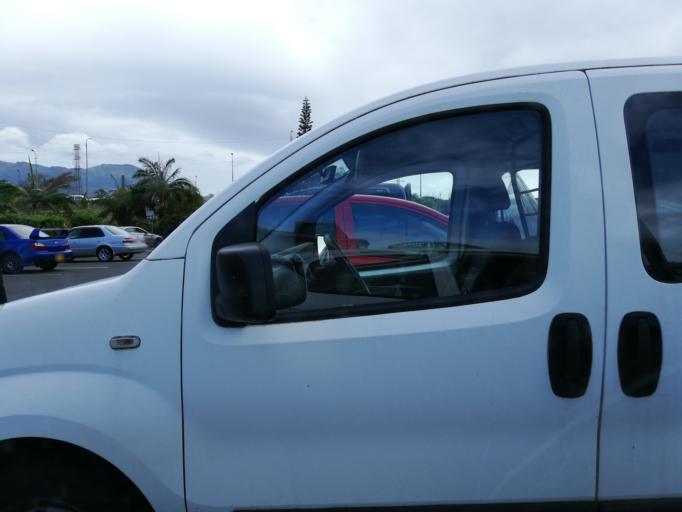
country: MU
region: Plaines Wilhems
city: Ebene
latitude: -20.2437
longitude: 57.4872
